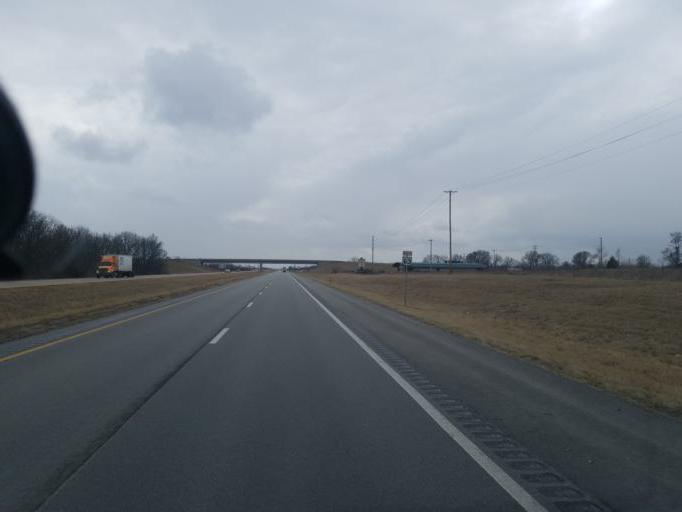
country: US
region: Missouri
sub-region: Randolph County
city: Moberly
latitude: 39.4116
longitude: -92.4124
